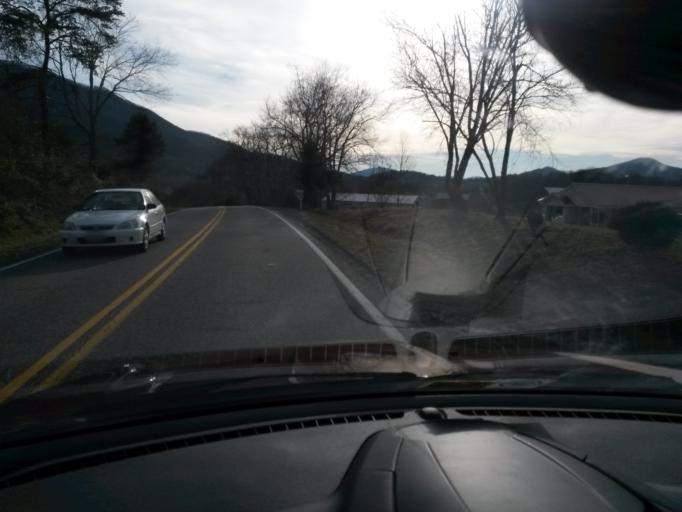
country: US
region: Virginia
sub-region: Bath County
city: Warm Springs
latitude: 37.9225
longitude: -79.7247
